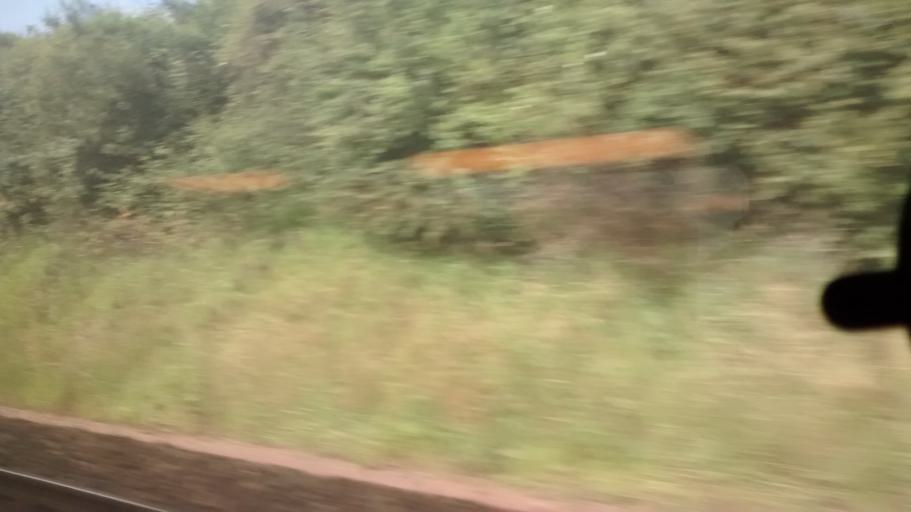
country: FR
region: Pays de la Loire
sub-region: Departement de la Sarthe
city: La Chapelle-Saint-Aubin
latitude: 48.0459
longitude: 0.1654
